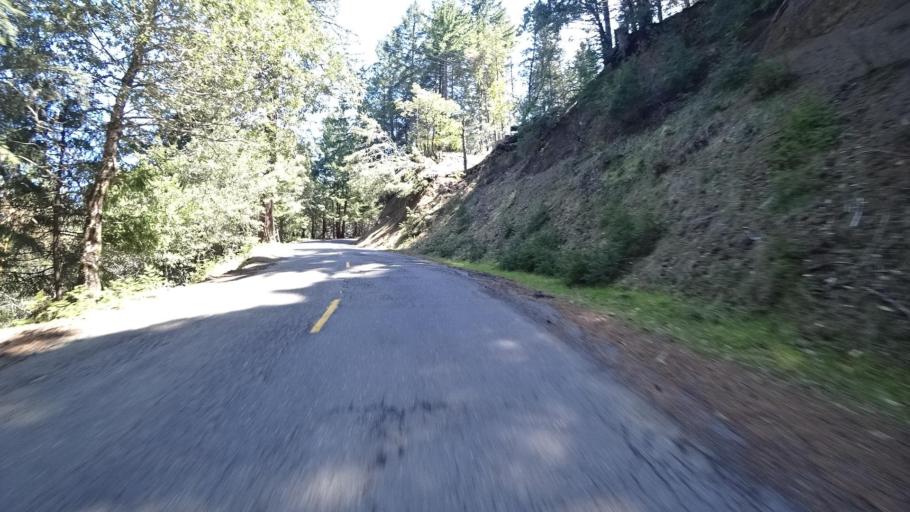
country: US
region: California
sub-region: Humboldt County
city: Rio Dell
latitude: 40.2922
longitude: -124.0570
